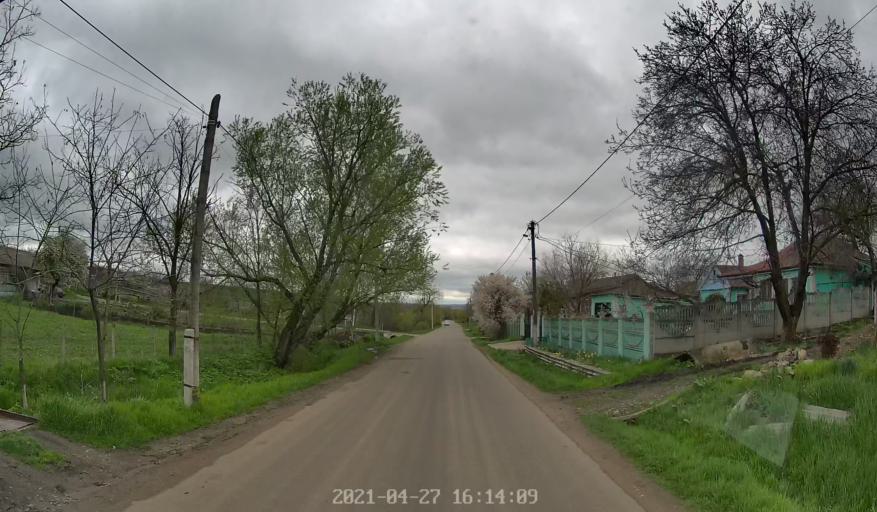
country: MD
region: Chisinau
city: Singera
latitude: 47.0045
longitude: 29.0148
